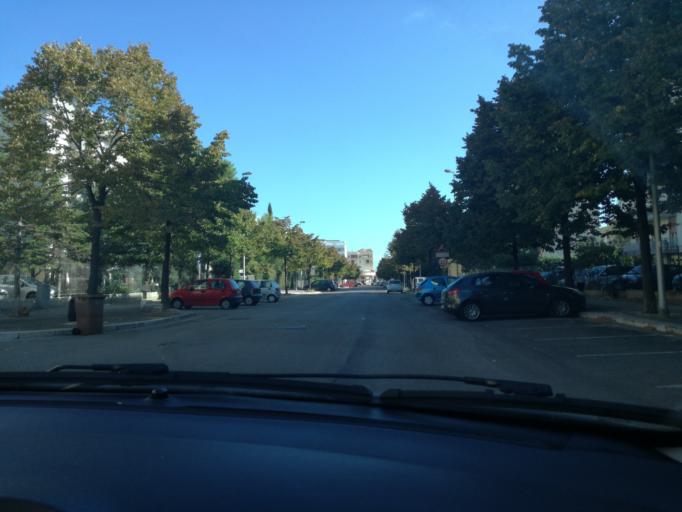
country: IT
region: Apulia
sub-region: Provincia di Bari
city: Triggiano
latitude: 41.0718
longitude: 16.9297
